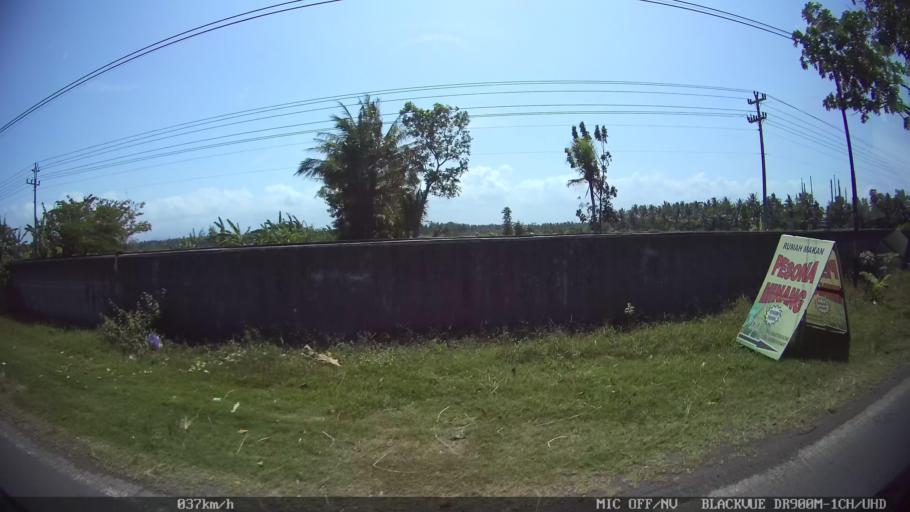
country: ID
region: Daerah Istimewa Yogyakarta
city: Srandakan
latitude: -7.9325
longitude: 110.1421
